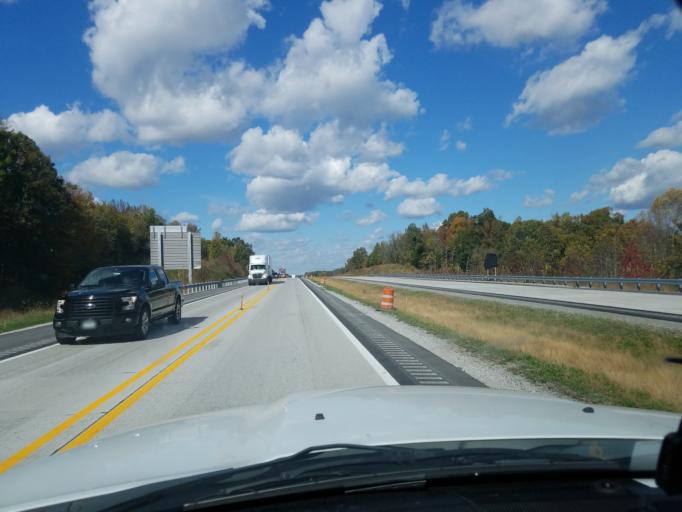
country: US
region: Kentucky
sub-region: Ohio County
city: Beaver Dam
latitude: 37.3958
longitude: -86.8170
